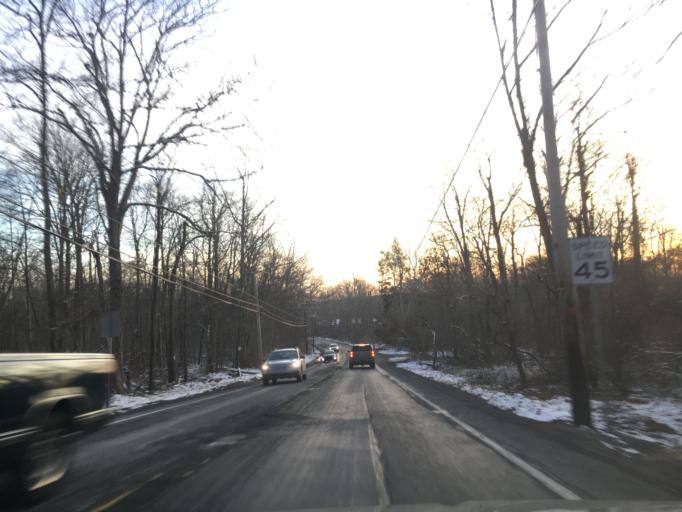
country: US
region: Pennsylvania
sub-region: Pike County
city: Saw Creek
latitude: 41.1212
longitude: -75.0931
